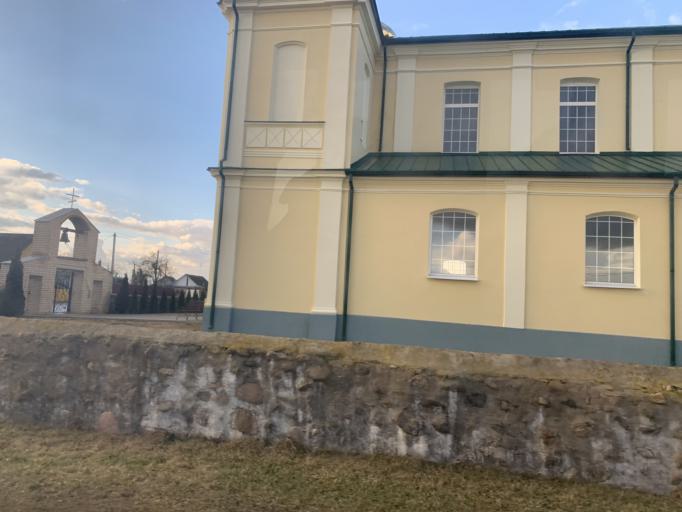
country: BY
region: Minsk
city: Novy Svyerzhan'
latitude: 53.3483
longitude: 26.6870
